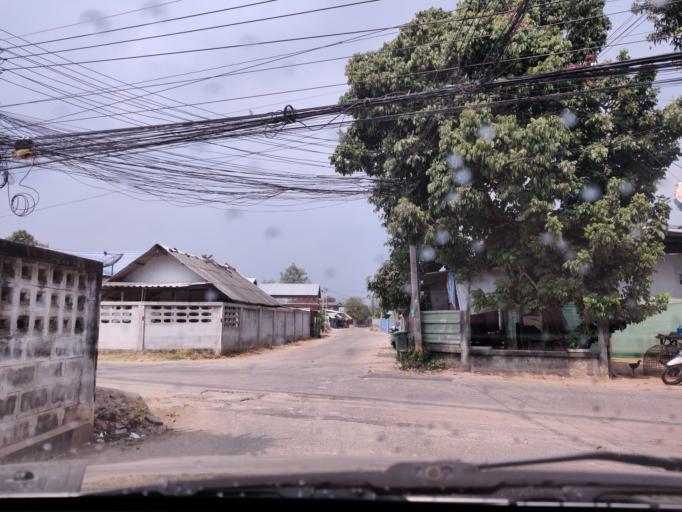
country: TH
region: Sisaket
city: Si Sa Ket
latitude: 15.1038
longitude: 104.3539
